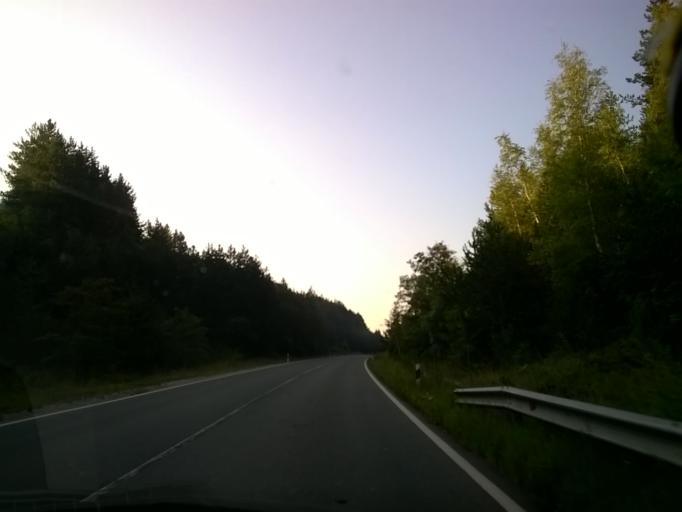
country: BG
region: Sofiya
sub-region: Obshtina Dragoman
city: Dragoman
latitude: 42.9433
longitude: 22.9041
